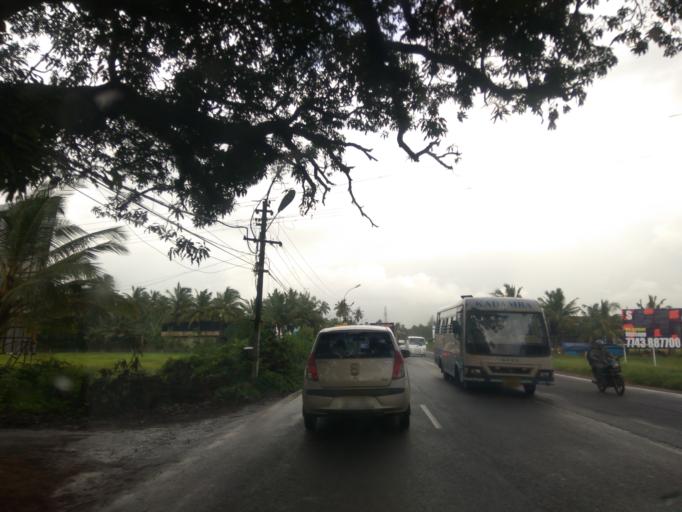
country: IN
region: Goa
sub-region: North Goa
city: Goa Velha
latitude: 15.4404
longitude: 73.8737
